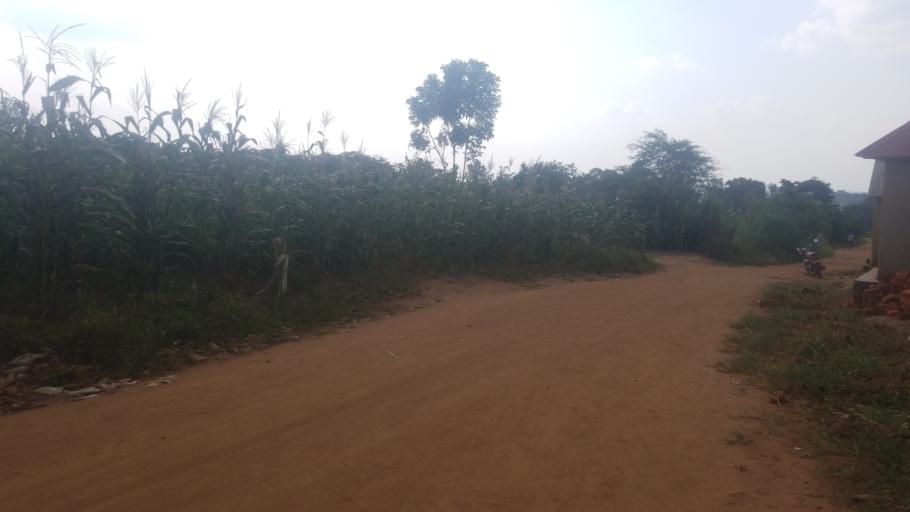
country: UG
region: Central Region
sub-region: Sembabule District
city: Sembabule
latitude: -0.0841
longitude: 31.4579
